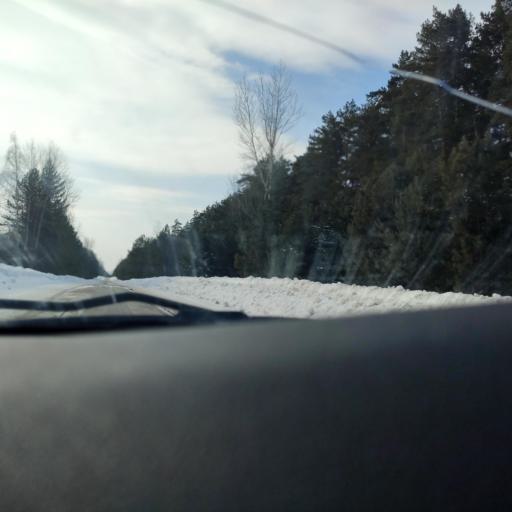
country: RU
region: Samara
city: Rozhdestveno
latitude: 53.2527
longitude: 49.9441
